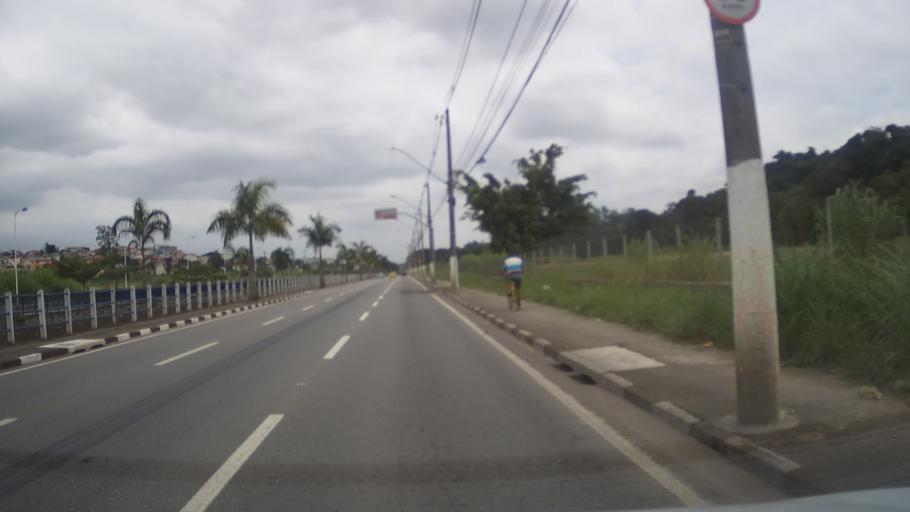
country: BR
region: Sao Paulo
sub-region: Aruja
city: Aruja
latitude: -23.3975
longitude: -46.3357
